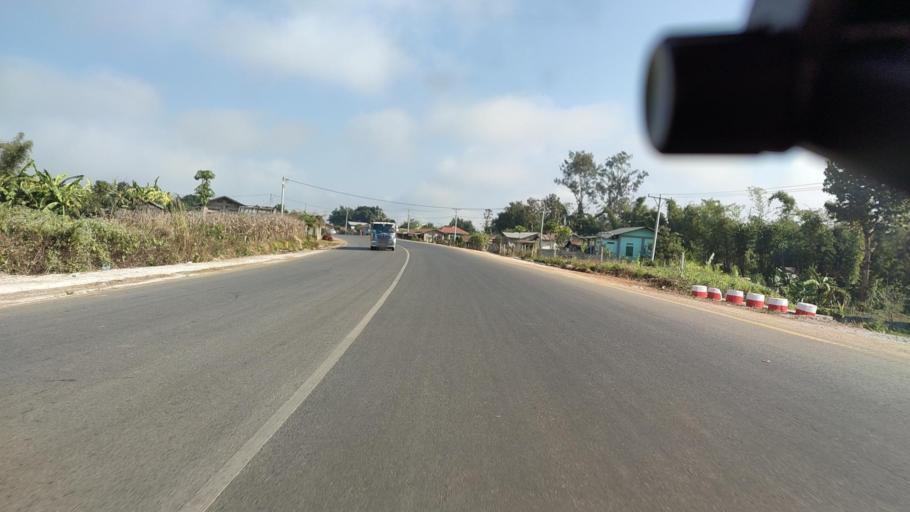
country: MM
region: Shan
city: Lashio
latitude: 23.1953
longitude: 97.8939
